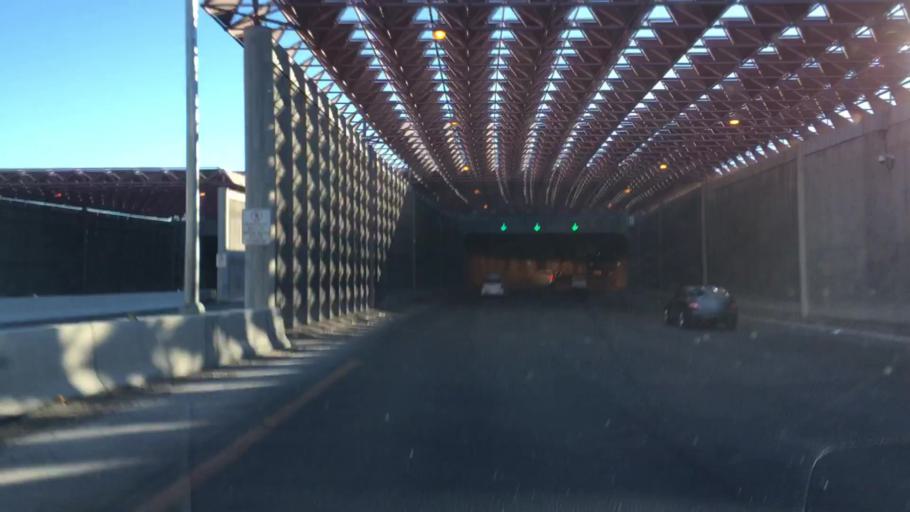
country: US
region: Nevada
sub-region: Clark County
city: Paradise
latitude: 36.0799
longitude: -115.1435
